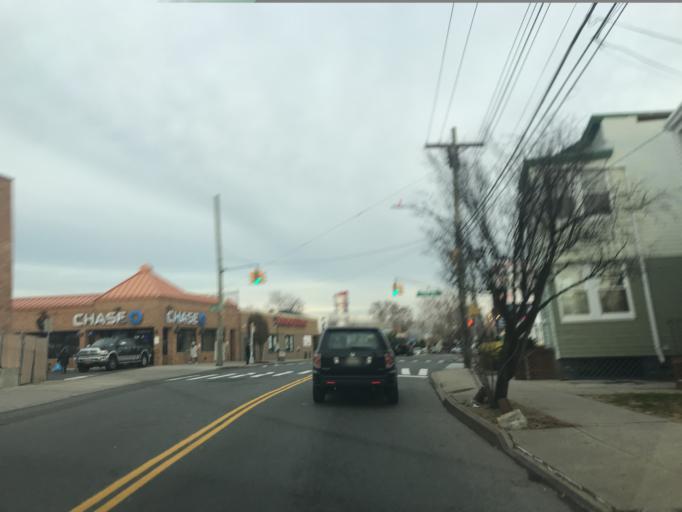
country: US
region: New York
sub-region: Bronx
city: The Bronx
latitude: 40.7862
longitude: -73.8368
